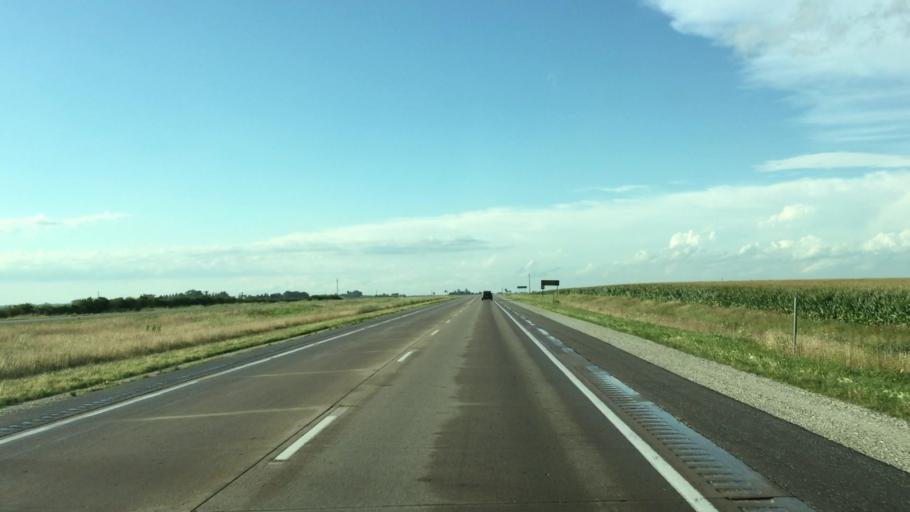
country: US
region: Iowa
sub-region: Henry County
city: Winfield
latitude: 41.1381
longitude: -91.5398
